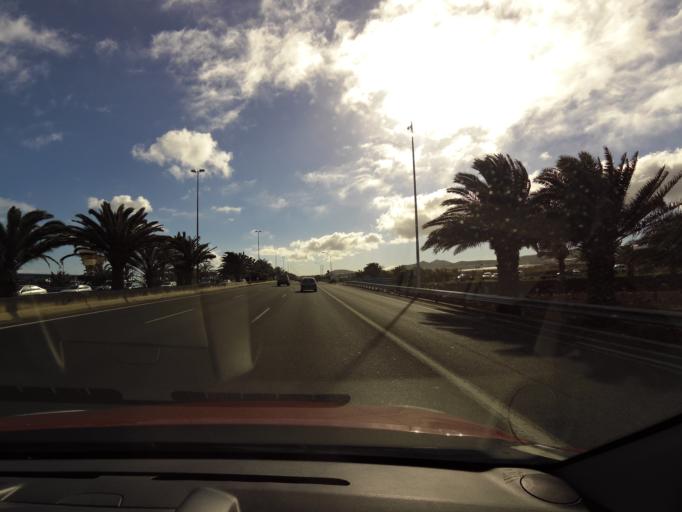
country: ES
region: Canary Islands
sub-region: Provincia de Las Palmas
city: Ingenio
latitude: 27.9399
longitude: -15.3911
